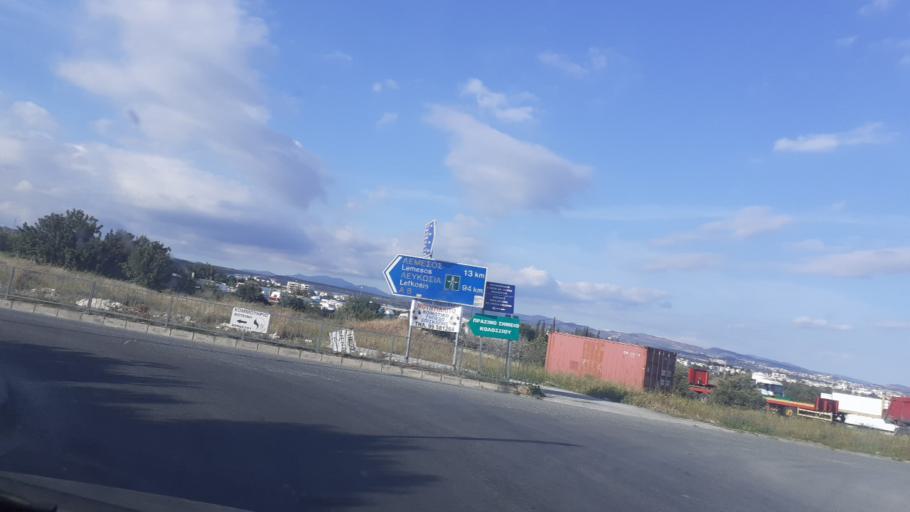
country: CY
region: Larnaka
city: Kolossi
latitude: 34.6850
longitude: 32.9400
